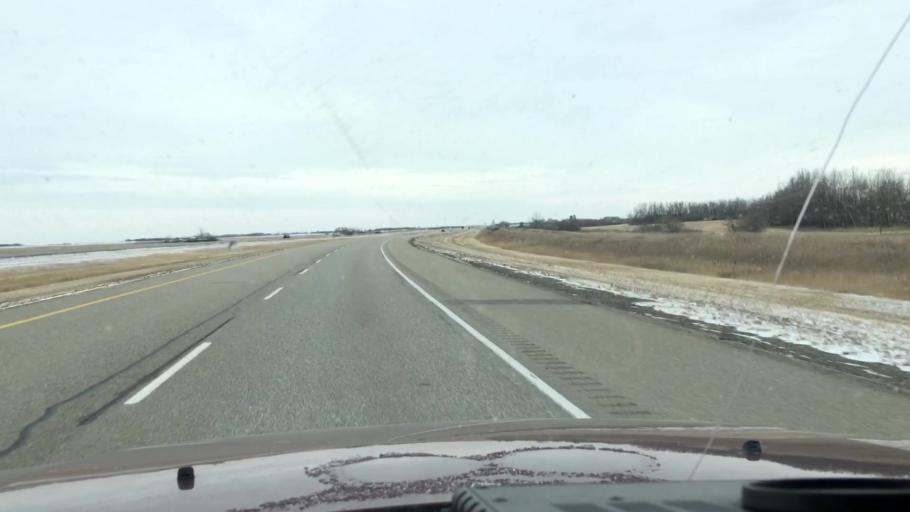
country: CA
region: Saskatchewan
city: Watrous
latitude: 51.3348
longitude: -106.0862
